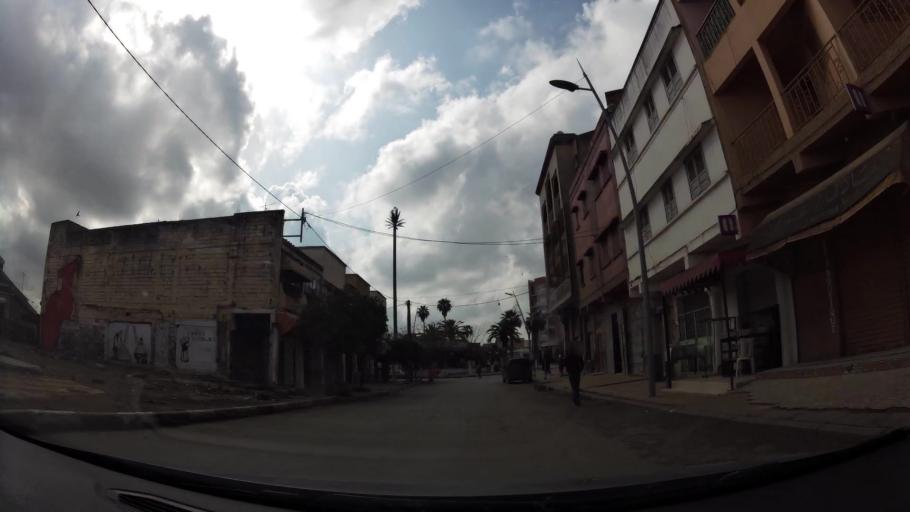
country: MA
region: Rabat-Sale-Zemmour-Zaer
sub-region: Khemisset
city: Tiflet
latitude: 33.8939
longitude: -6.3107
